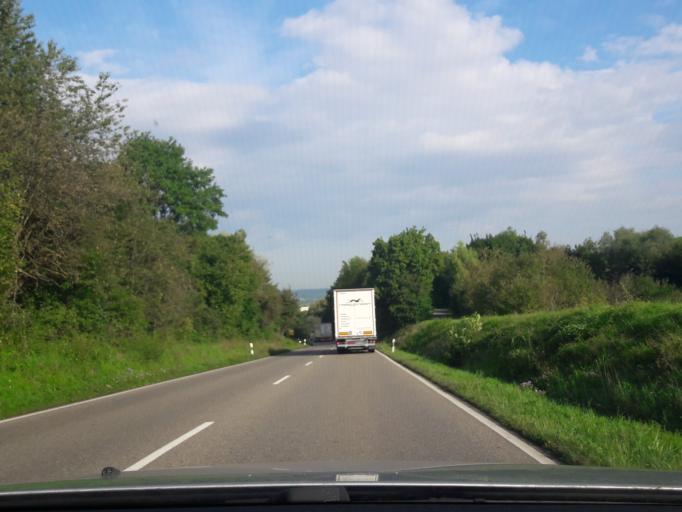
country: DE
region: Baden-Wuerttemberg
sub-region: Regierungsbezirk Stuttgart
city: Grossbottwar
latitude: 48.9900
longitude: 9.3061
